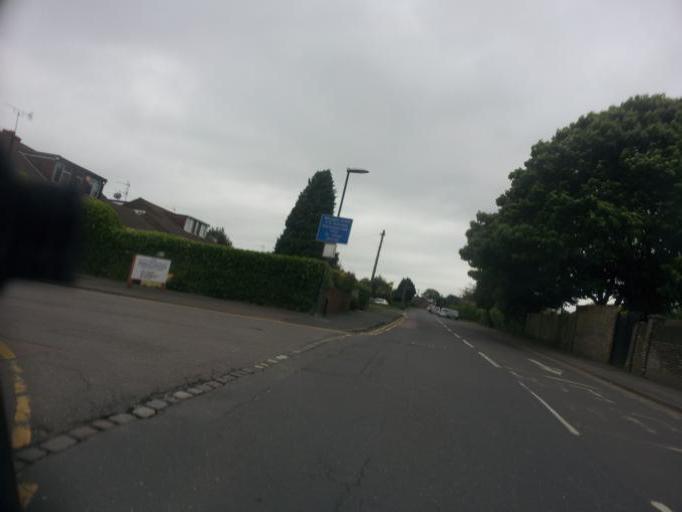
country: GB
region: England
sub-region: Kent
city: Maidstone
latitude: 51.2523
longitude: 0.5275
